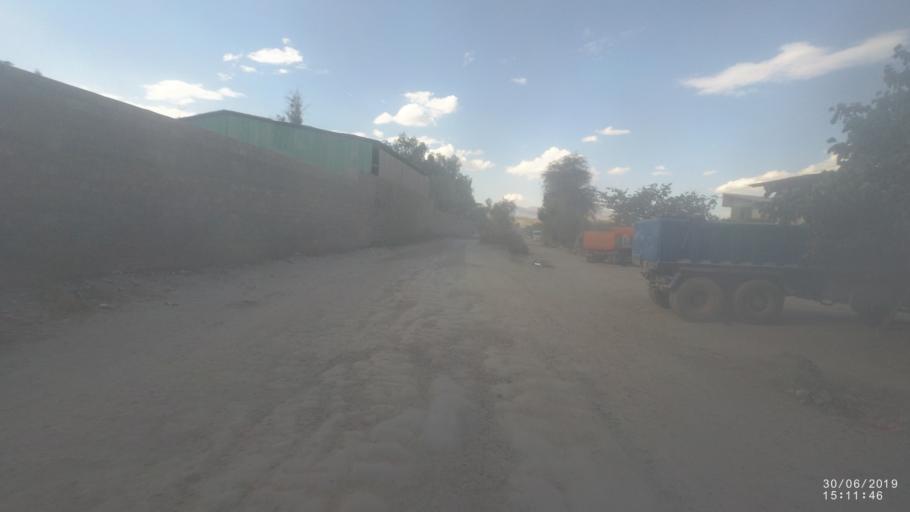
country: BO
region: Cochabamba
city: Irpa Irpa
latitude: -17.7266
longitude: -66.2901
